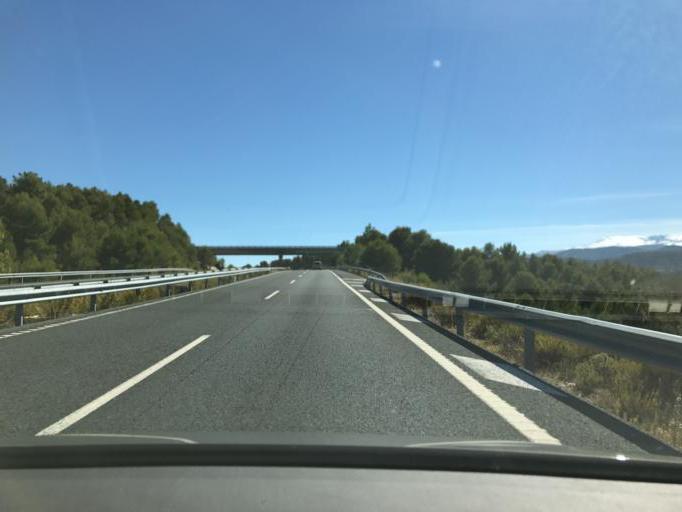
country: ES
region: Andalusia
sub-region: Provincia de Granada
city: Diezma
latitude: 37.3093
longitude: -3.3741
